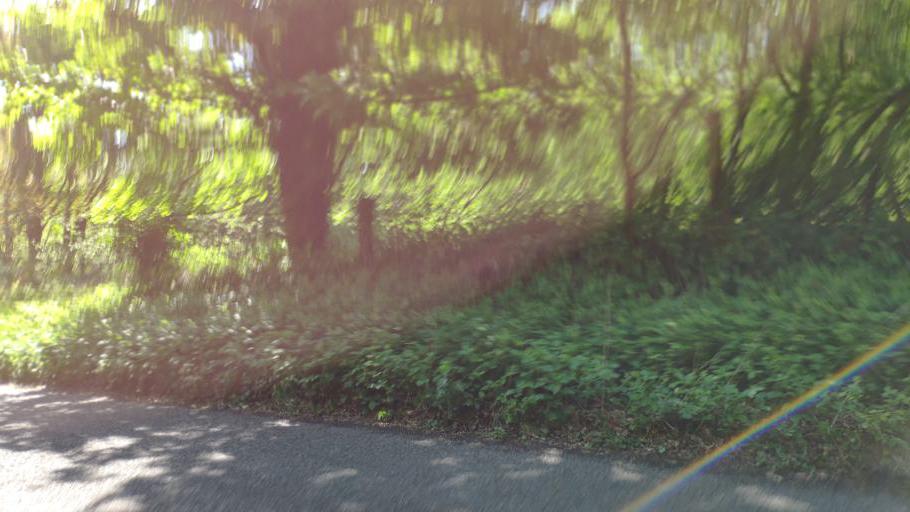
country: IE
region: Munster
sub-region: County Cork
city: Blarney
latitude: 51.9740
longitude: -8.5809
